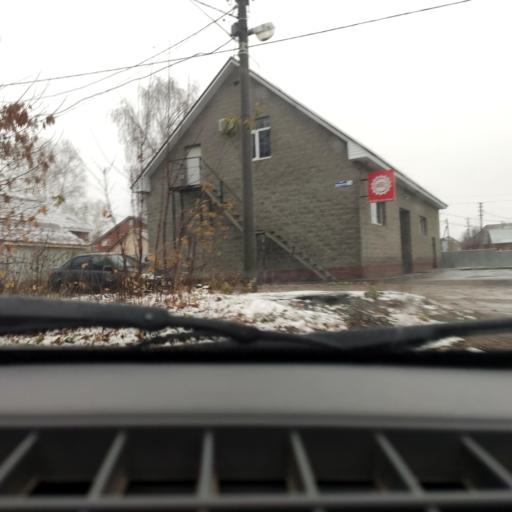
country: RU
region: Bashkortostan
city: Avdon
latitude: 54.6874
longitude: 55.7922
